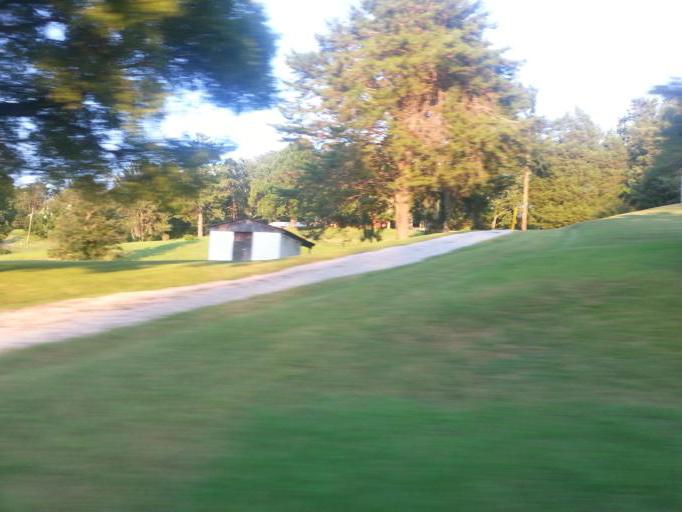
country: US
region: Tennessee
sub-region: Roane County
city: Kingston
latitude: 35.8594
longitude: -84.5261
